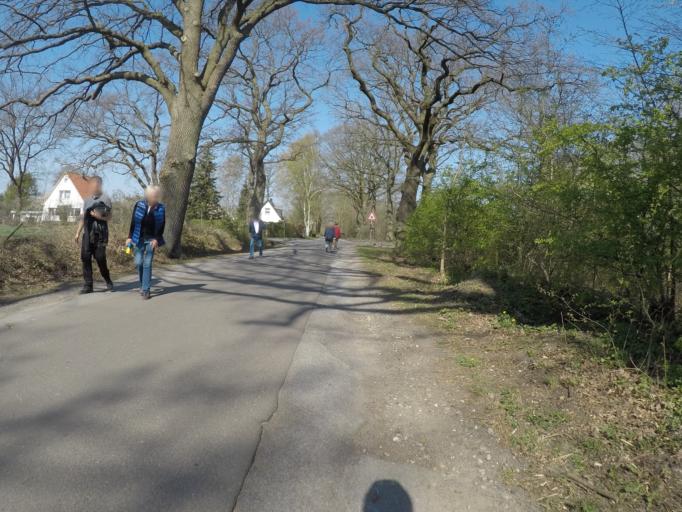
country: DE
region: Schleswig-Holstein
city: Halstenbek
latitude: 53.5960
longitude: 9.8138
